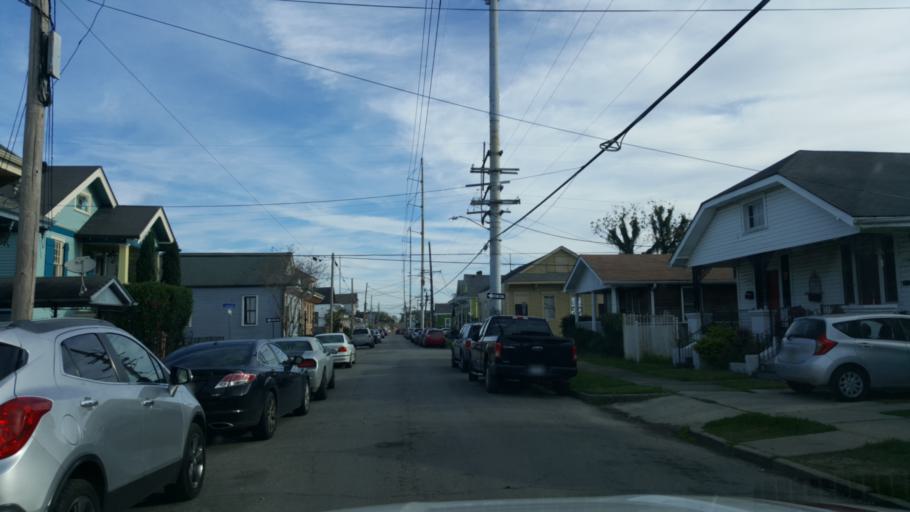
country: US
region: Louisiana
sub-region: Orleans Parish
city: New Orleans
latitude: 29.9731
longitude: -90.0696
